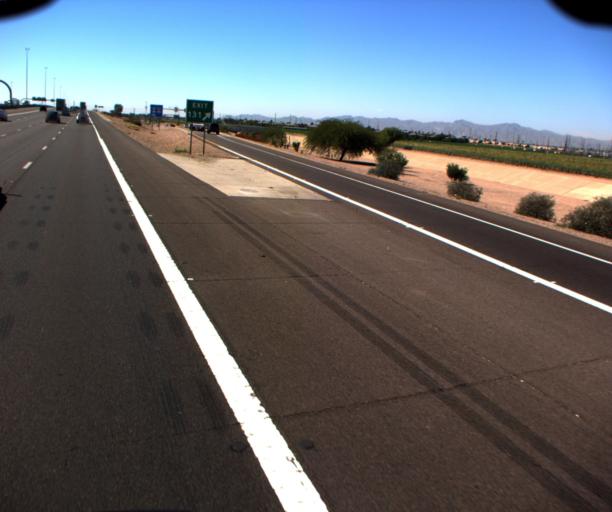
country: US
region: Arizona
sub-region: Maricopa County
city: Tolleson
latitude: 33.4603
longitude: -112.3022
